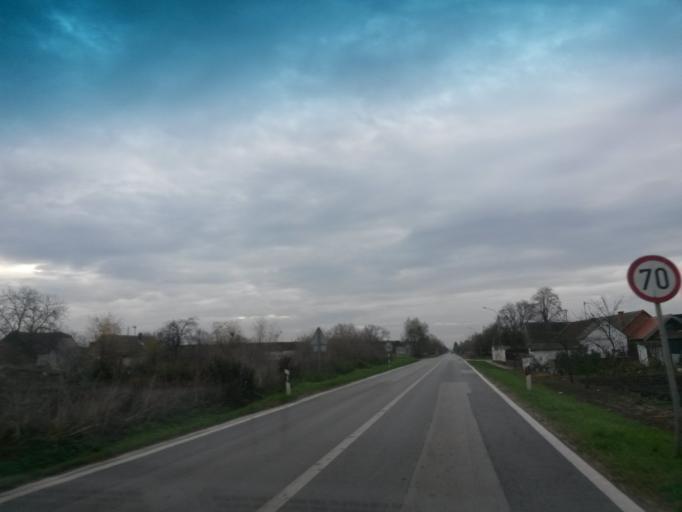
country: HR
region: Vukovarsko-Srijemska
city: Trpinja
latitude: 45.4264
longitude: 18.8952
